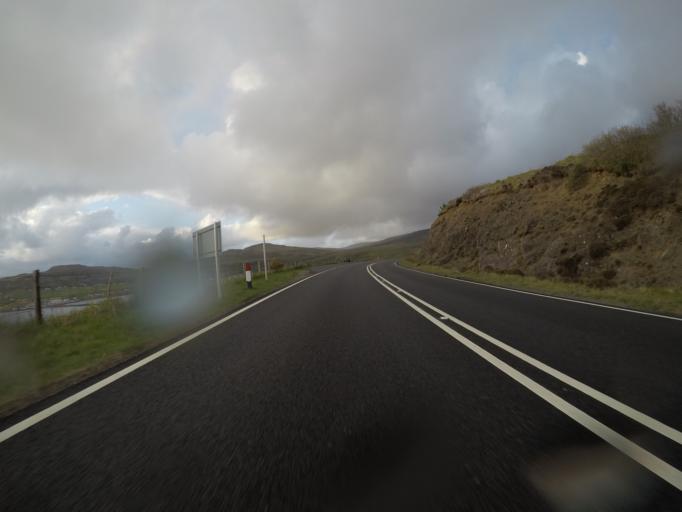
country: GB
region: Scotland
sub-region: Highland
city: Portree
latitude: 57.5775
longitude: -6.3653
